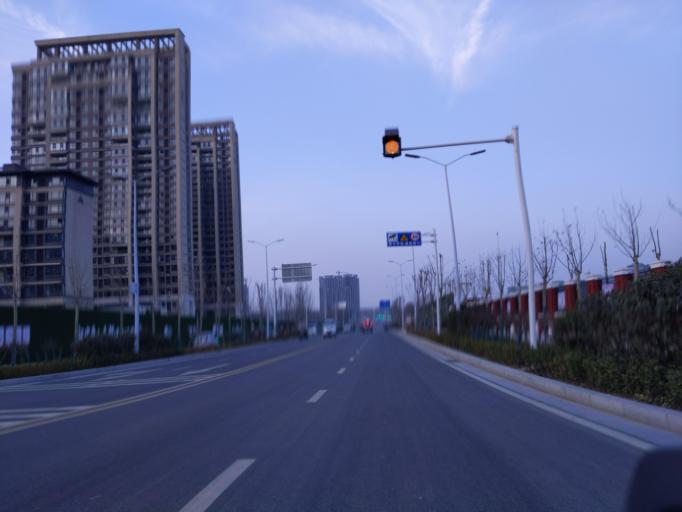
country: CN
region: Henan Sheng
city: Puyang
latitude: 35.8075
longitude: 115.0113
